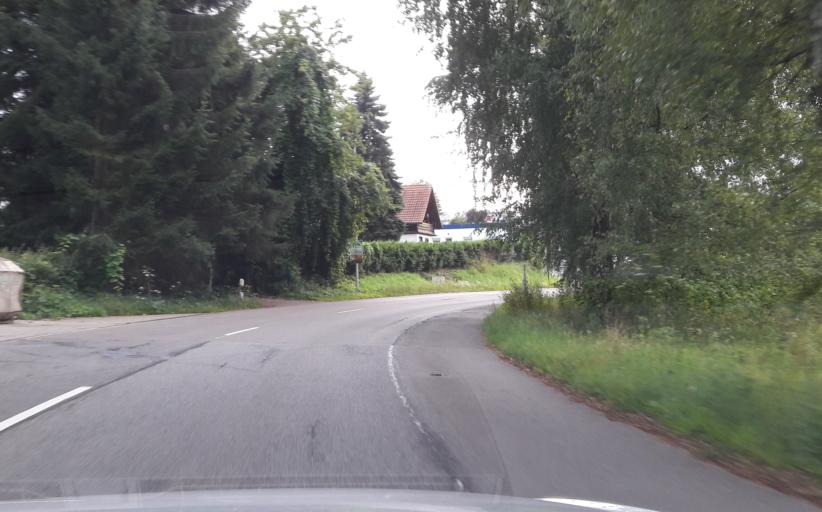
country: DE
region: Saarland
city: Bexbach
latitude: 49.3427
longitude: 7.2496
